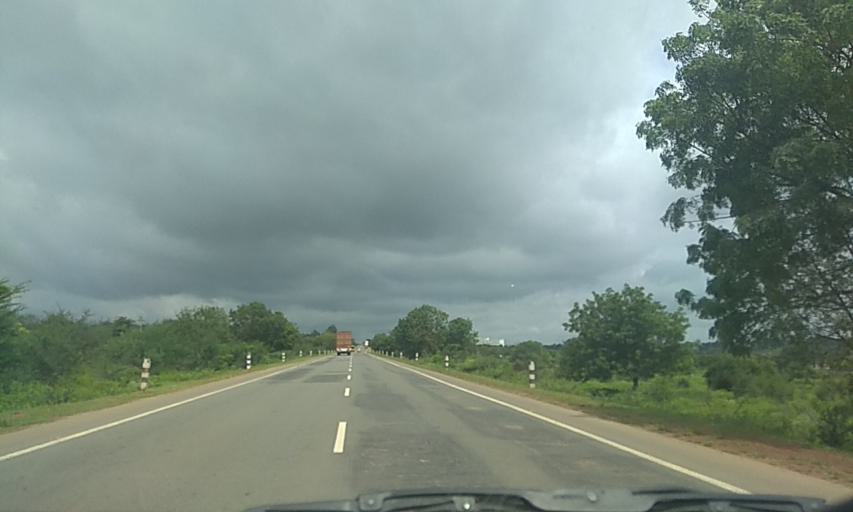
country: IN
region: Karnataka
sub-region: Dharwad
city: Hubli
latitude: 15.3388
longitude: 75.0866
